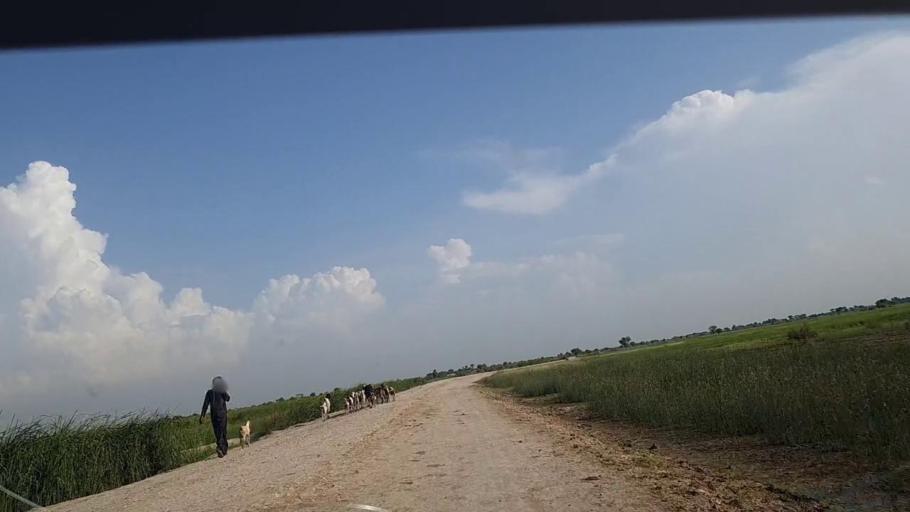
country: PK
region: Sindh
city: Khanpur
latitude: 27.8563
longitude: 69.3768
